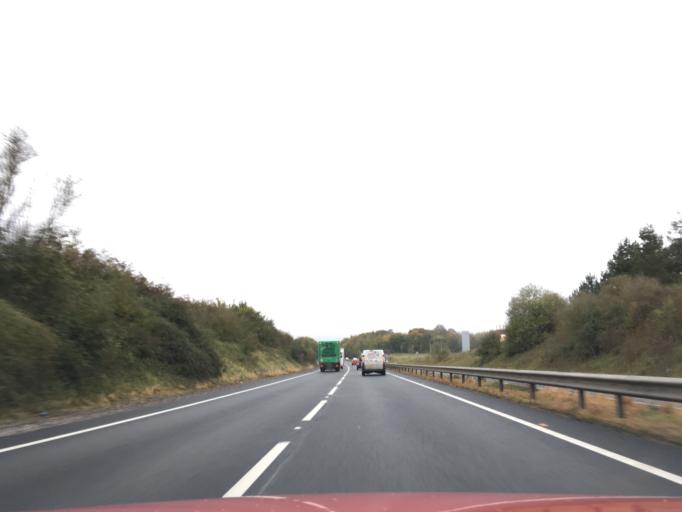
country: GB
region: England
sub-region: Hampshire
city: Kings Worthy
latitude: 51.1572
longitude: -1.3450
